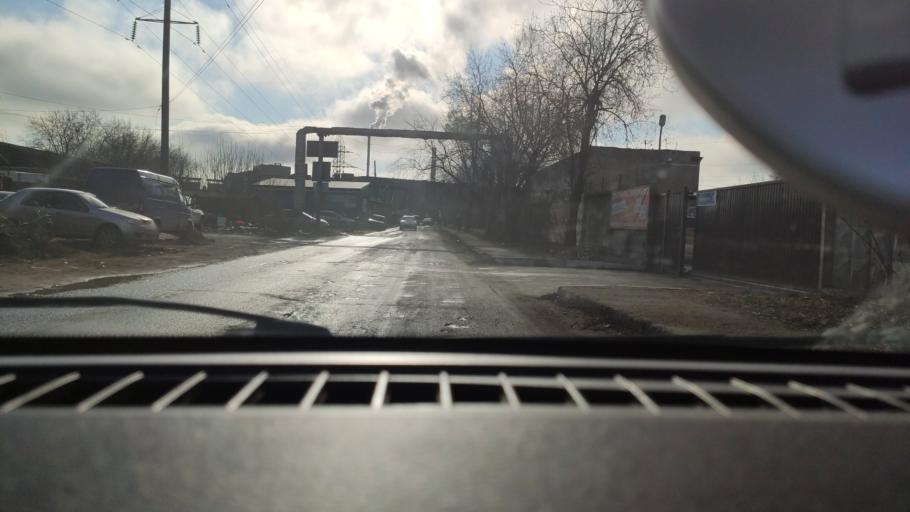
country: RU
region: Perm
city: Perm
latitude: 57.9825
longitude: 56.2401
